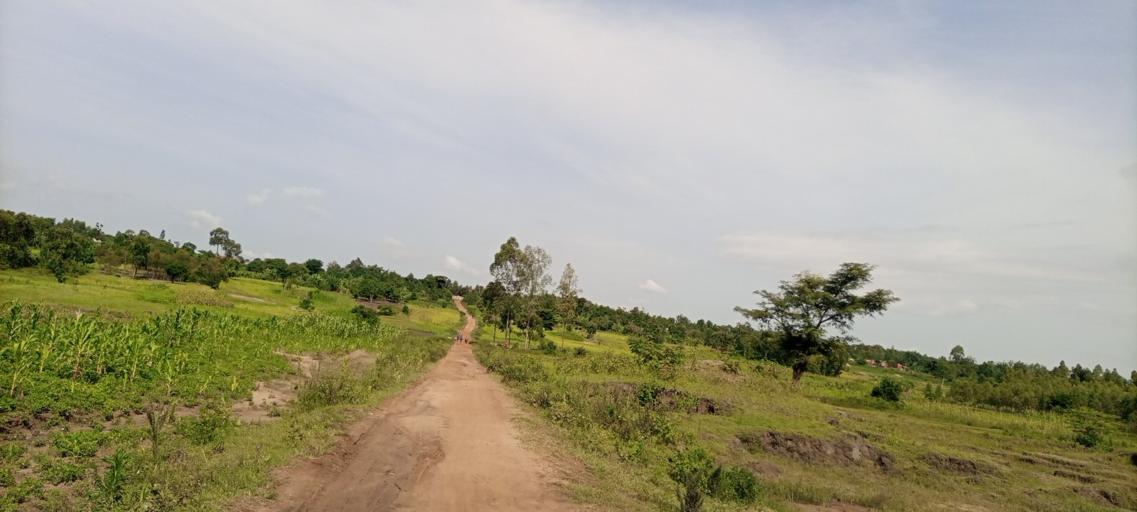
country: UG
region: Eastern Region
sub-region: Mbale District
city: Mbale
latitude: 1.1286
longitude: 34.0359
